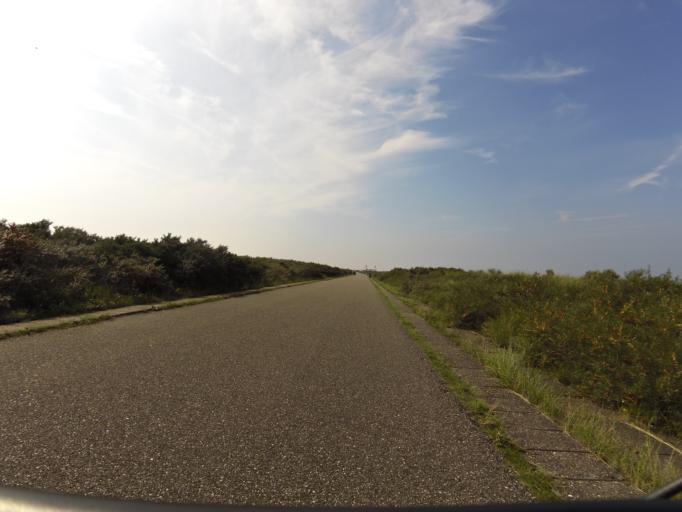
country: NL
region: Zeeland
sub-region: Gemeente Veere
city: Veere
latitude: 51.5902
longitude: 3.6501
